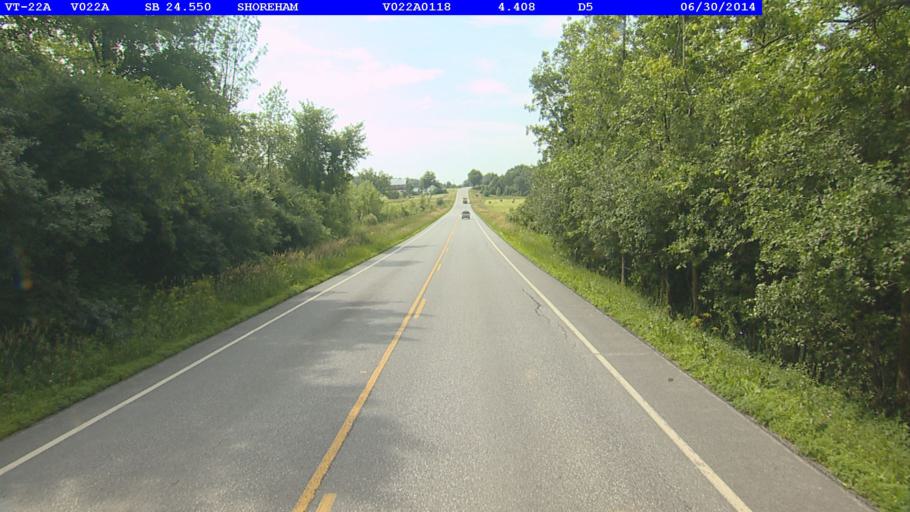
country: US
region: New York
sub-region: Essex County
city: Ticonderoga
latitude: 43.9127
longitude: -73.3115
